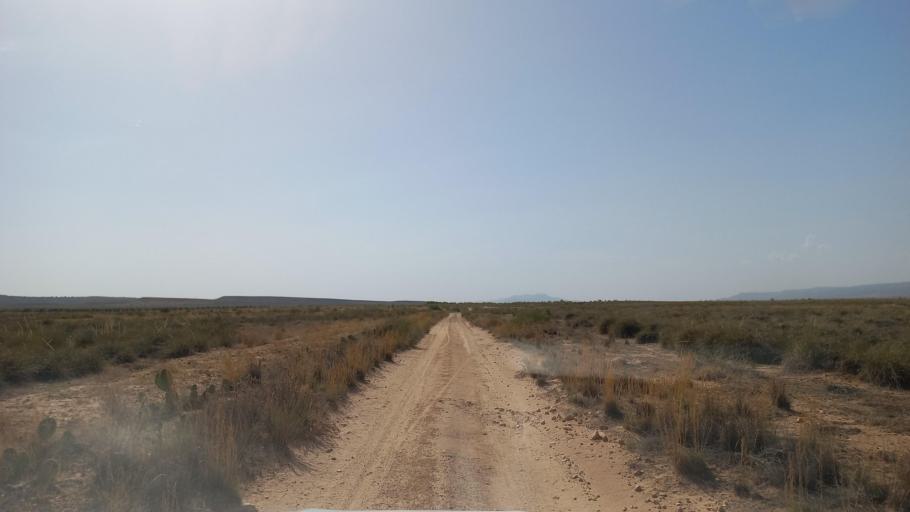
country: TN
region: Al Qasrayn
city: Kasserine
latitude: 35.2165
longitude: 9.0257
